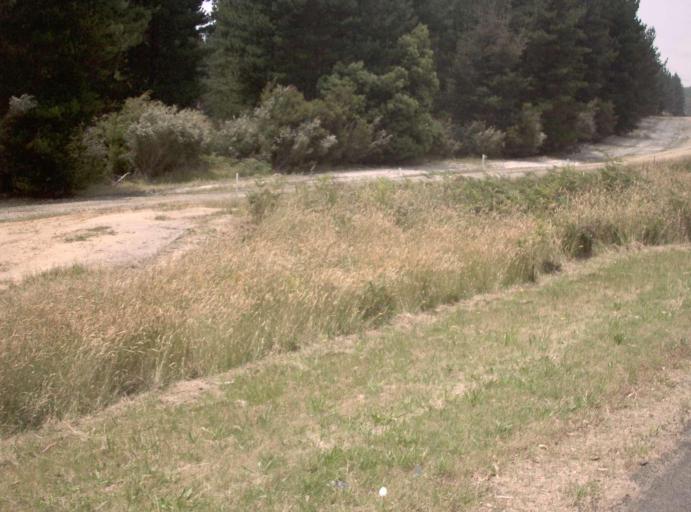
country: AU
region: Victoria
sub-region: Latrobe
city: Traralgon
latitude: -38.2606
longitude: 146.6799
